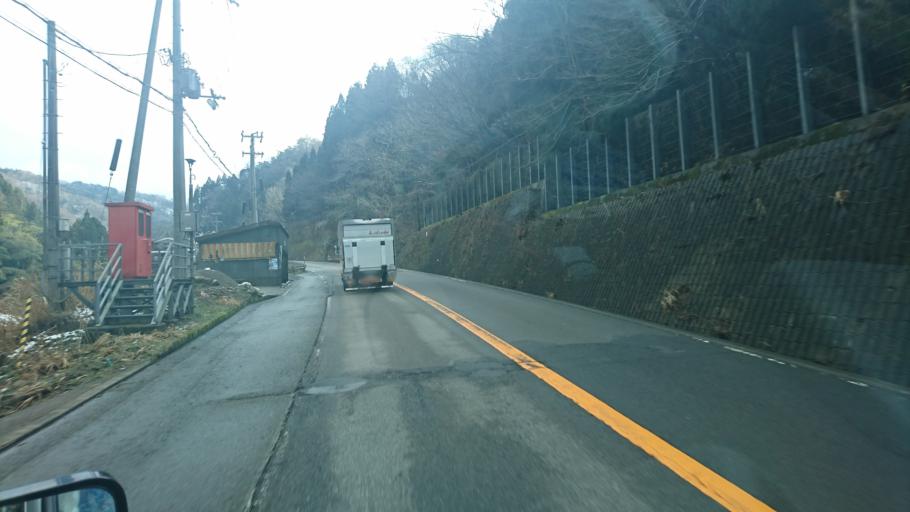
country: JP
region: Tottori
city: Tottori
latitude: 35.5274
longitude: 134.5181
